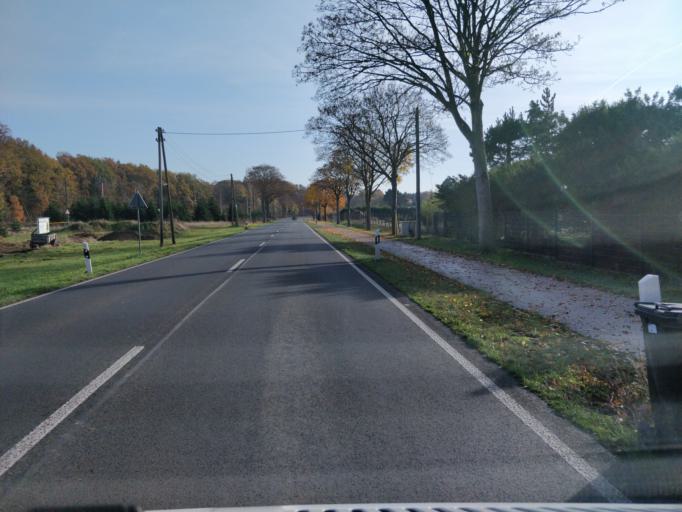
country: DE
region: North Rhine-Westphalia
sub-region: Regierungsbezirk Dusseldorf
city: Mehrhoog
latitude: 51.7645
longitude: 6.4659
